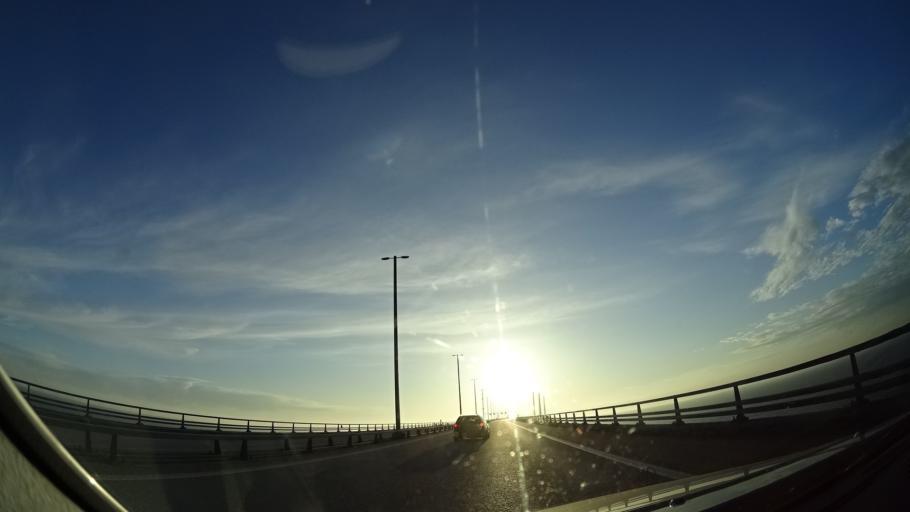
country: SE
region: Skane
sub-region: Malmo
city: Bunkeflostrand
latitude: 55.5678
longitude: 12.8673
